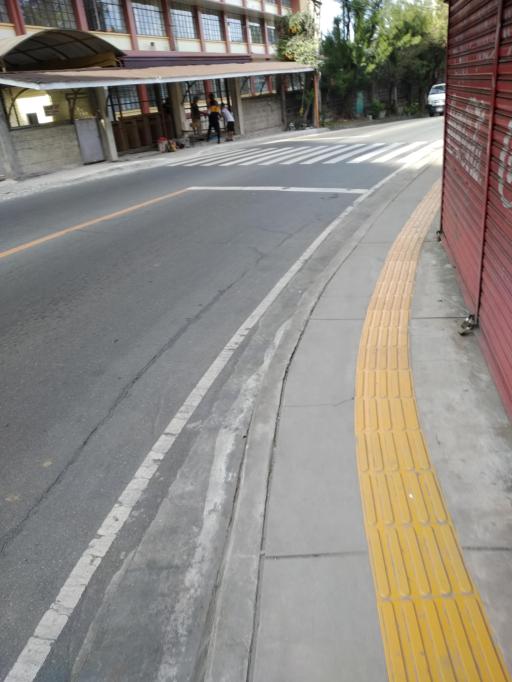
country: PH
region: Cordillera
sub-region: Baguio City
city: Baguio
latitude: 16.4172
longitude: 120.5986
